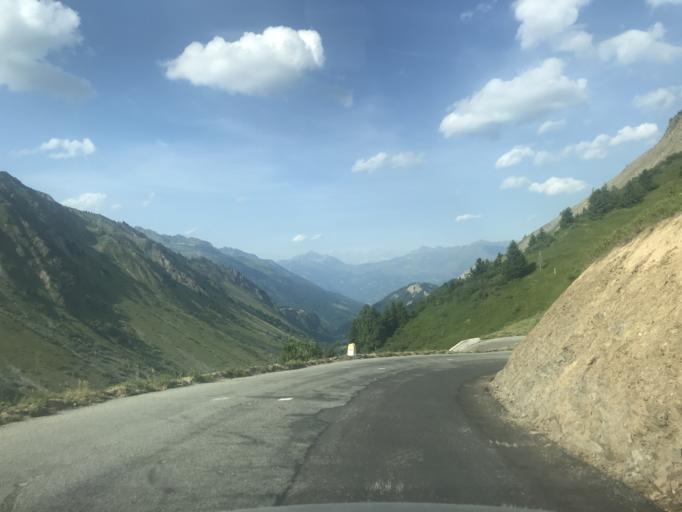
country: FR
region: Rhone-Alpes
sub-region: Departement de la Savoie
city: Saint-Etienne-de-Cuines
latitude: 45.2425
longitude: 6.1747
